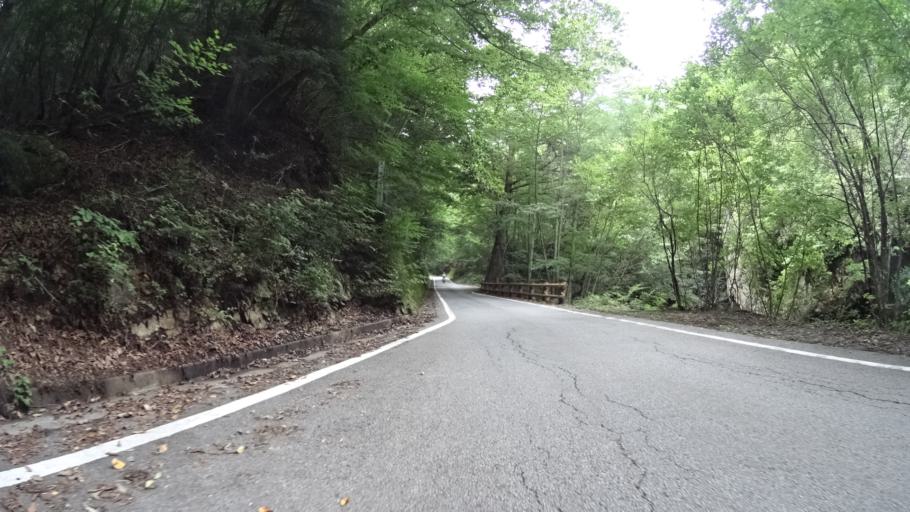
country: JP
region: Yamanashi
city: Nirasaki
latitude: 35.8636
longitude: 138.5528
